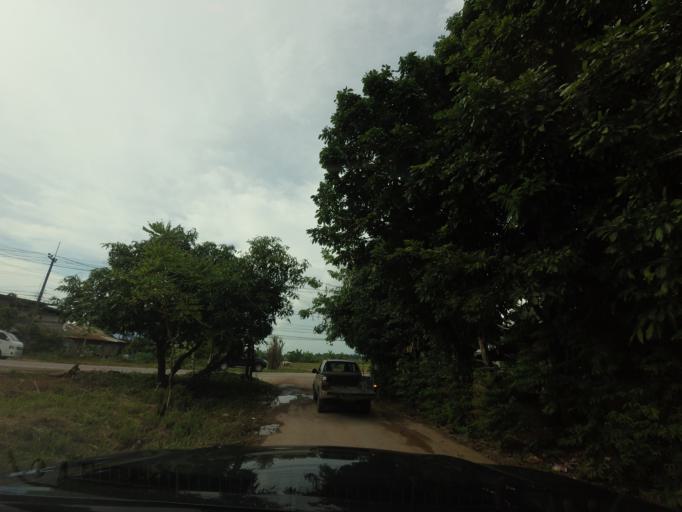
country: TH
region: Changwat Nong Bua Lamphu
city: Suwannakhuha
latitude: 17.4188
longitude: 102.3347
